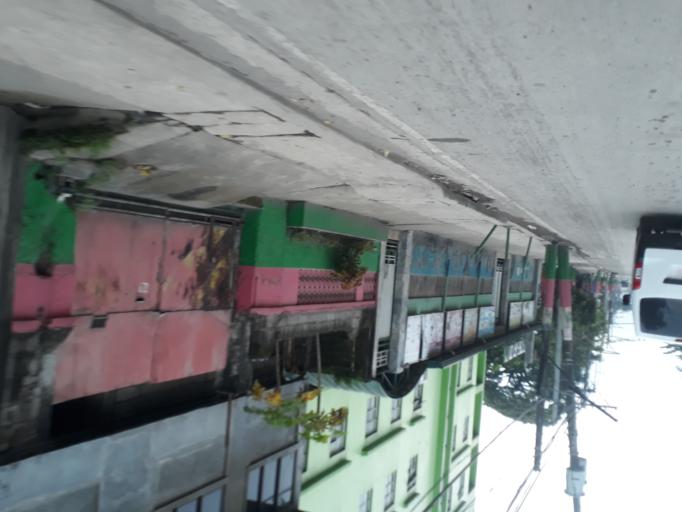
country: PH
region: Calabarzon
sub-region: Province of Rizal
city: Valenzuela
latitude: 14.6909
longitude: 120.9561
